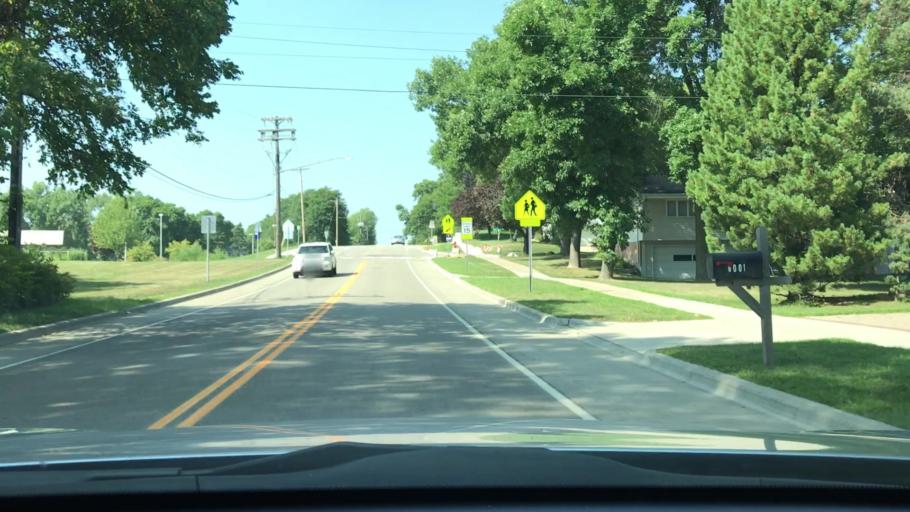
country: US
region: Minnesota
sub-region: Hennepin County
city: Edina
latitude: 44.8950
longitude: -93.3679
